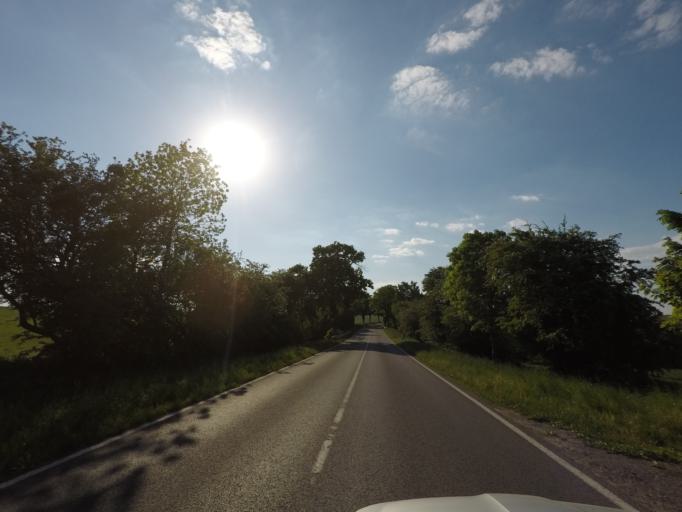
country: DE
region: Brandenburg
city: Hohenfinow
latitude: 52.8057
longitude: 13.9379
